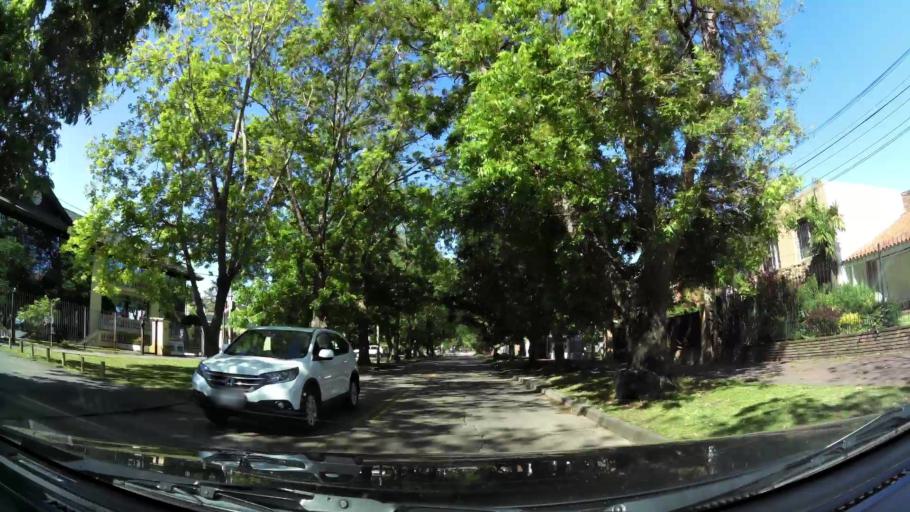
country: UY
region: Canelones
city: Paso de Carrasco
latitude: -34.8891
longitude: -56.0668
